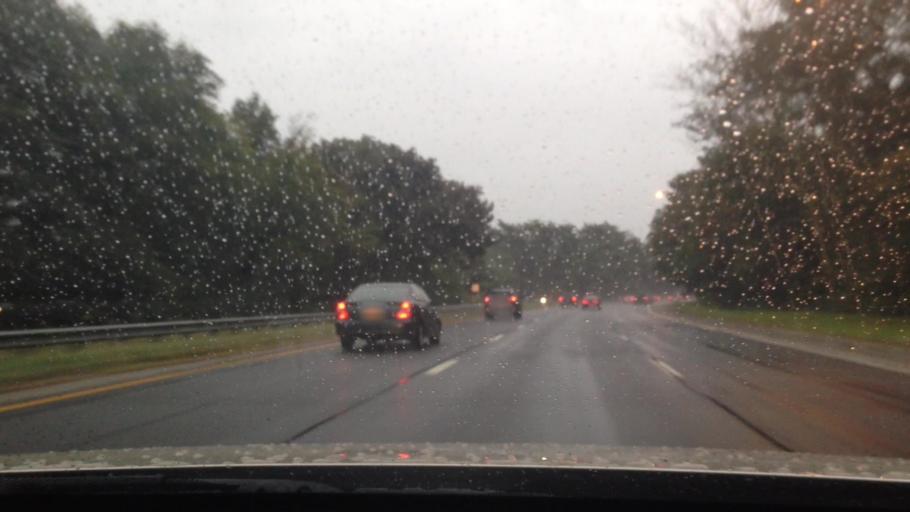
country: US
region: New York
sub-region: Suffolk County
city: West Babylon
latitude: 40.7321
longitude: -73.3577
